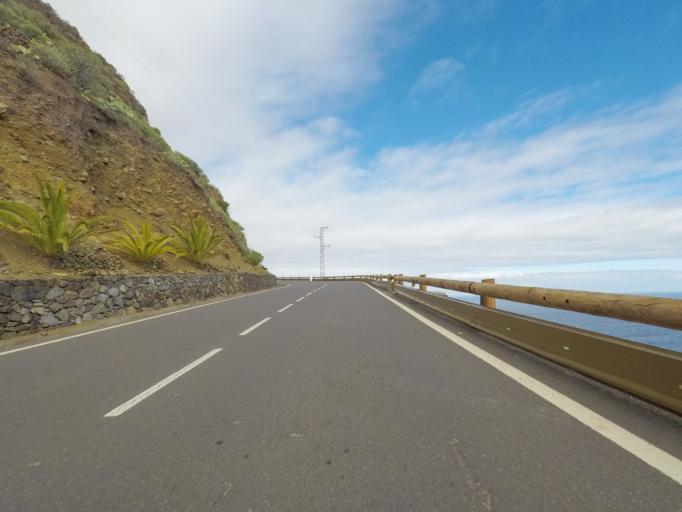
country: ES
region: Canary Islands
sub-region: Provincia de Santa Cruz de Tenerife
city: Agulo
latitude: 28.1842
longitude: -17.1877
